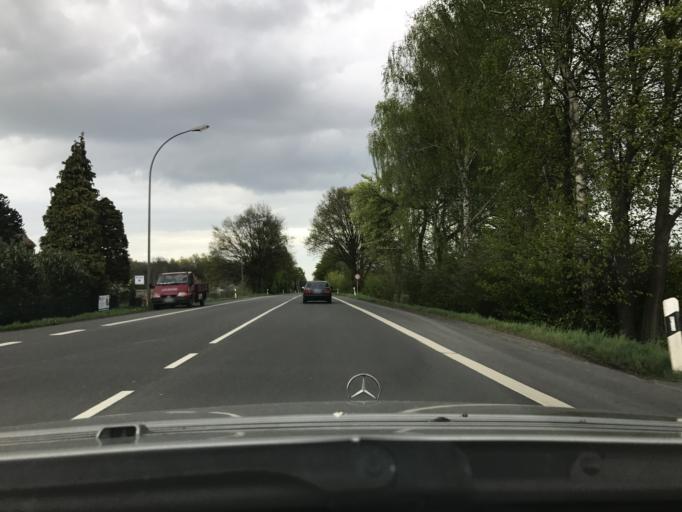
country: DE
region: North Rhine-Westphalia
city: Lunen
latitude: 51.5863
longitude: 7.4701
